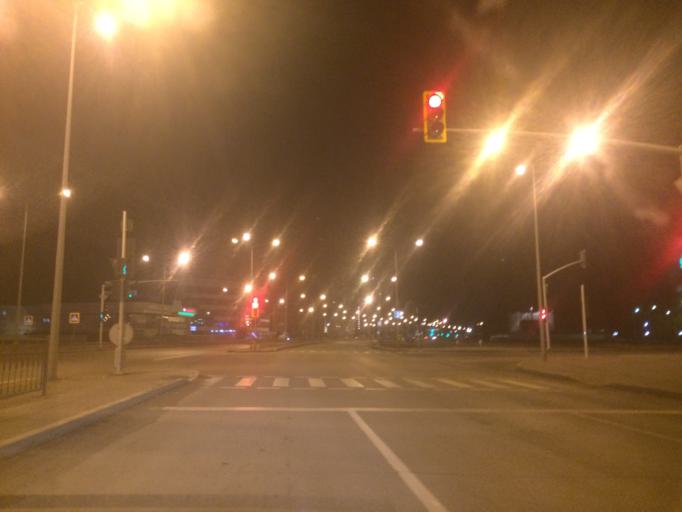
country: KZ
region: Astana Qalasy
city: Astana
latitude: 51.1469
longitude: 71.3747
